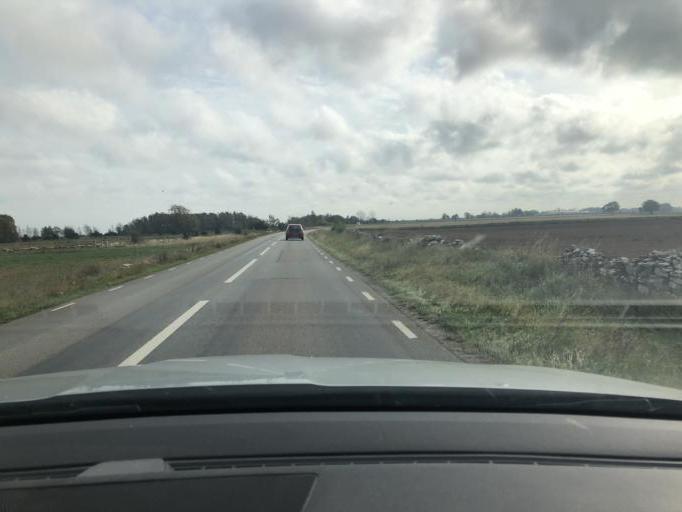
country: SE
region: Kalmar
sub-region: Morbylanga Kommun
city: Moerbylanga
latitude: 56.4372
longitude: 16.4331
